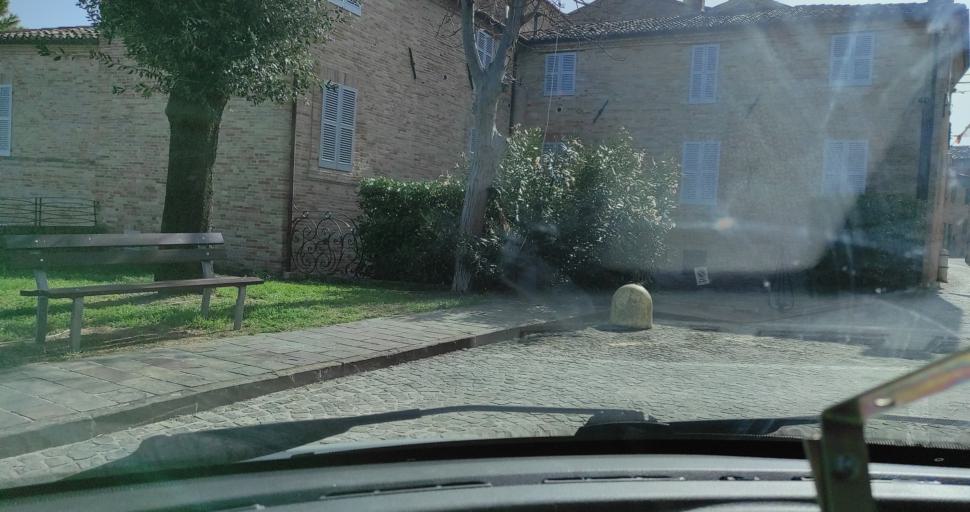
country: IT
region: The Marches
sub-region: Provincia di Macerata
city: Loro Piceno
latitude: 43.1679
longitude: 13.4167
